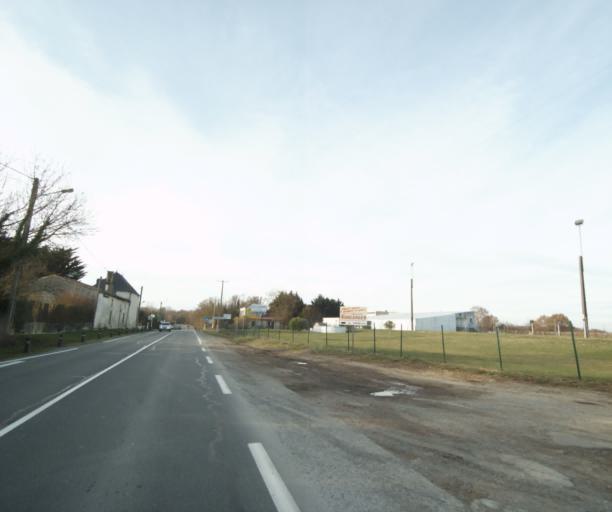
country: FR
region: Poitou-Charentes
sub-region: Departement de la Charente-Maritime
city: Chaniers
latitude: 45.7449
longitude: -0.5600
